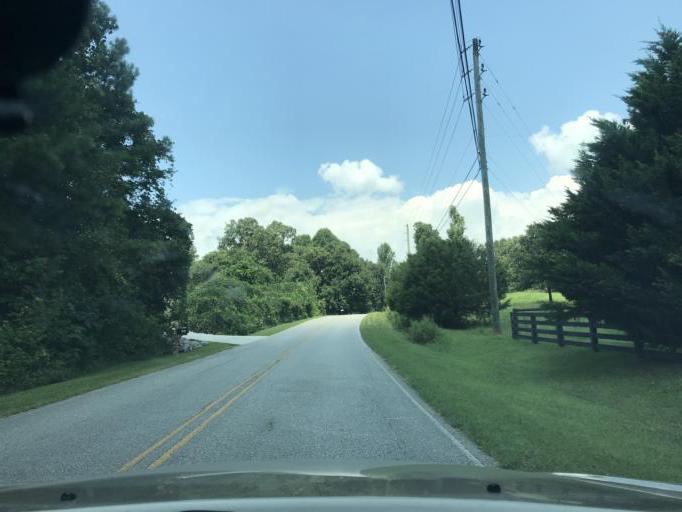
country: US
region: Georgia
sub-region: Dawson County
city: Dawsonville
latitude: 34.3442
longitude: -84.0822
